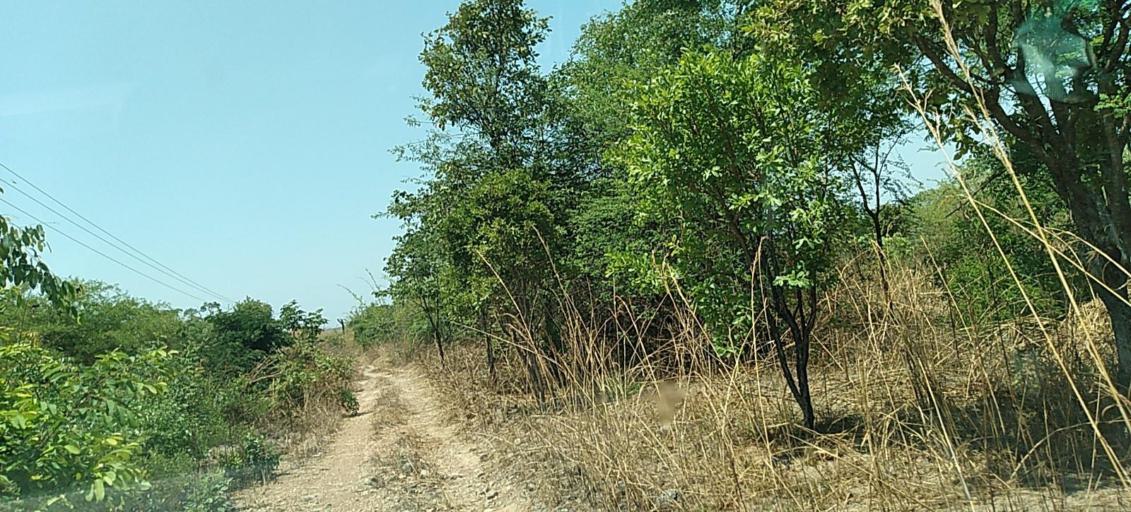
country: ZM
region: Copperbelt
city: Luanshya
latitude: -12.9798
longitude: 28.3294
